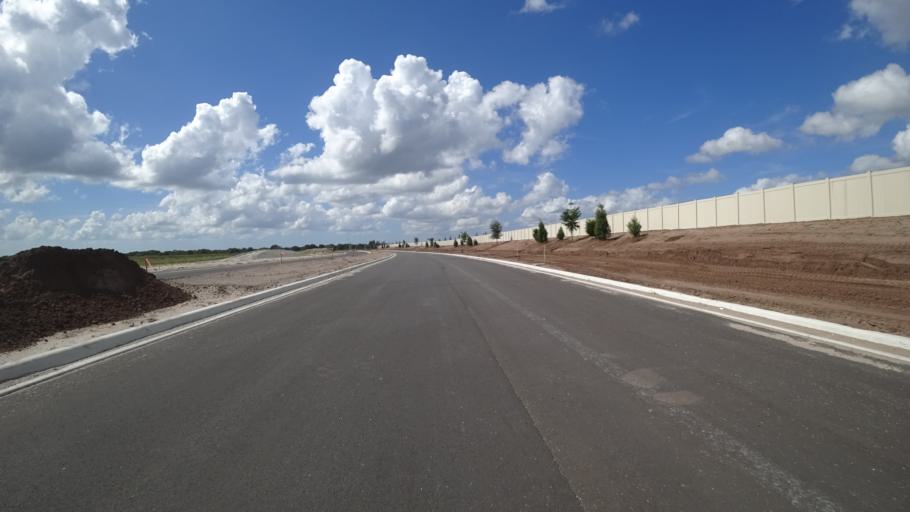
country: US
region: Florida
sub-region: Sarasota County
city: The Meadows
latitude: 27.4546
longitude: -82.3851
